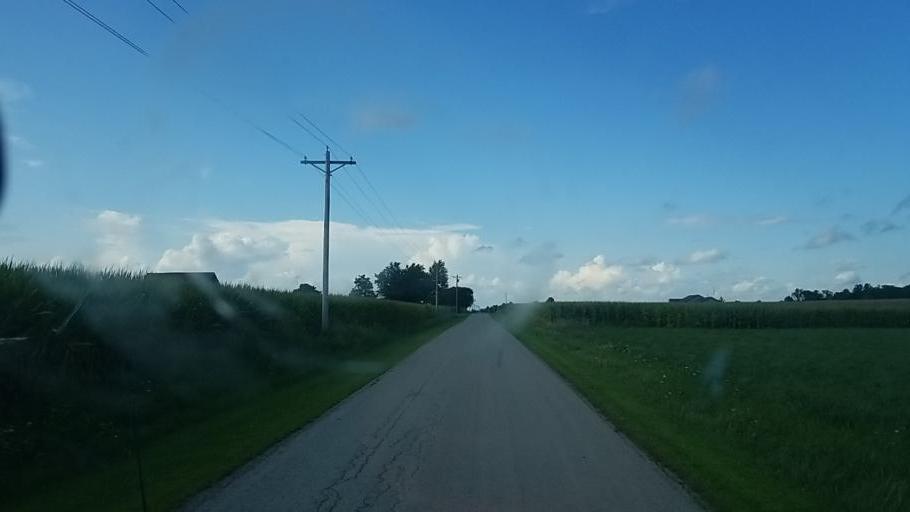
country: US
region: Ohio
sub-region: Hardin County
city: Forest
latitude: 40.7901
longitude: -83.3999
